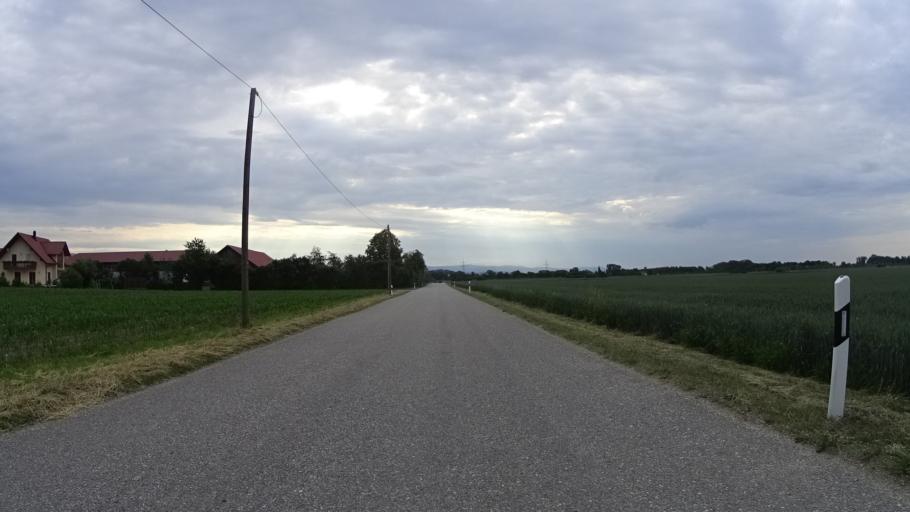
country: DE
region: Bavaria
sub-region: Lower Bavaria
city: Kirchroth
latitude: 48.9408
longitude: 12.5329
